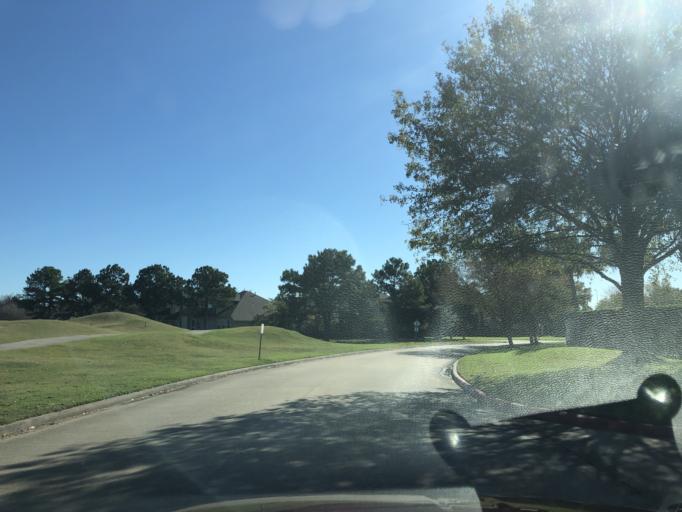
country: US
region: Texas
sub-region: Harris County
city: Oak Cliff Place
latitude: 29.9413
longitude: -95.6635
